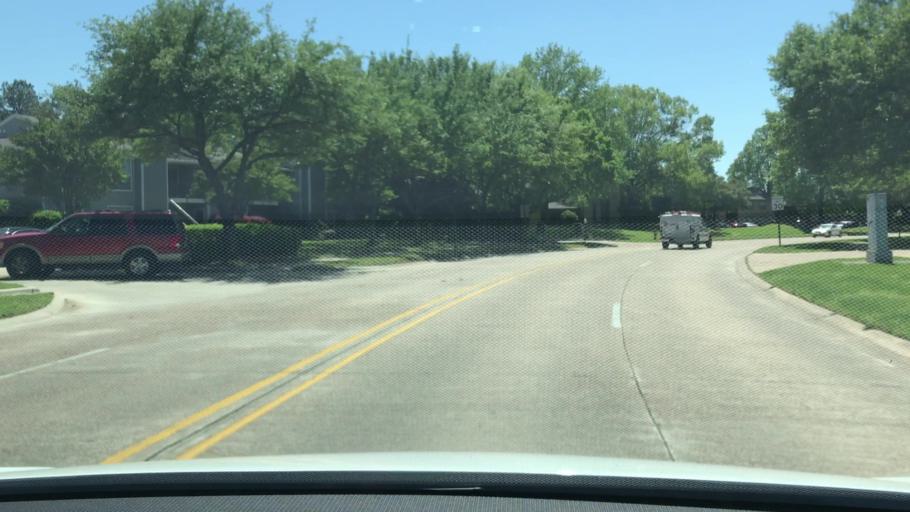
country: US
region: Louisiana
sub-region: Bossier Parish
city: Bossier City
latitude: 32.4249
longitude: -93.7104
